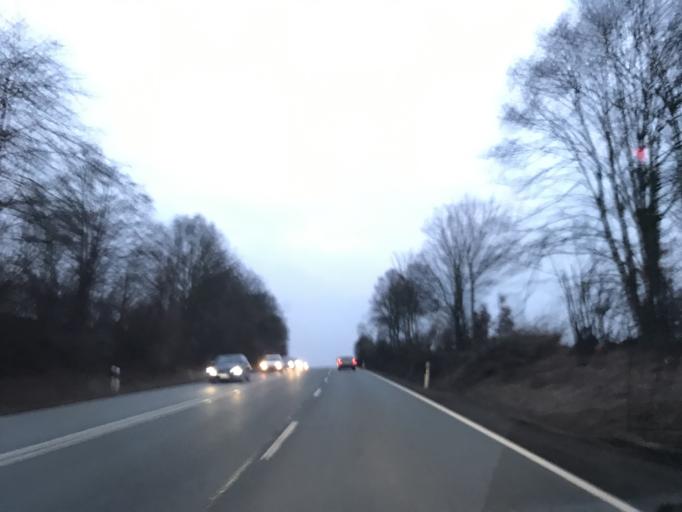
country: DE
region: Hesse
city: Grebenstein
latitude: 51.4589
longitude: 9.4077
